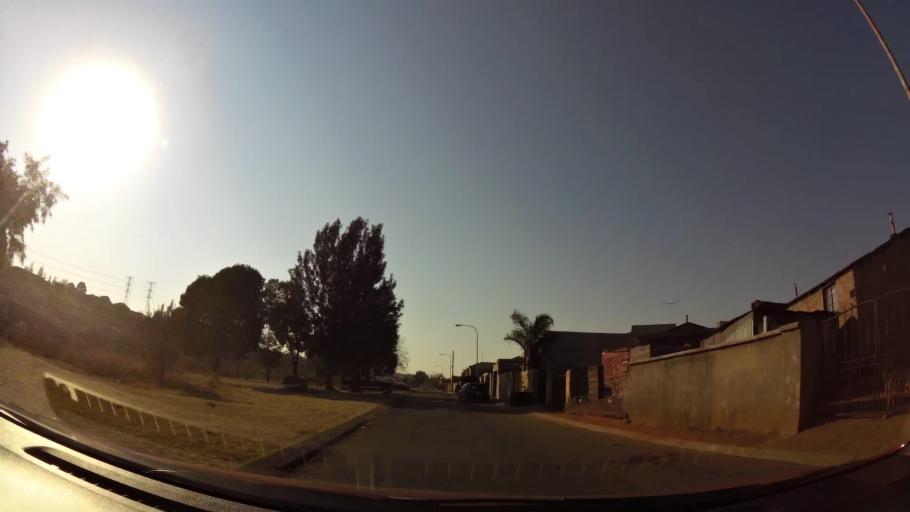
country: ZA
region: Gauteng
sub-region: City of Johannesburg Metropolitan Municipality
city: Soweto
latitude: -26.2561
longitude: 27.9468
